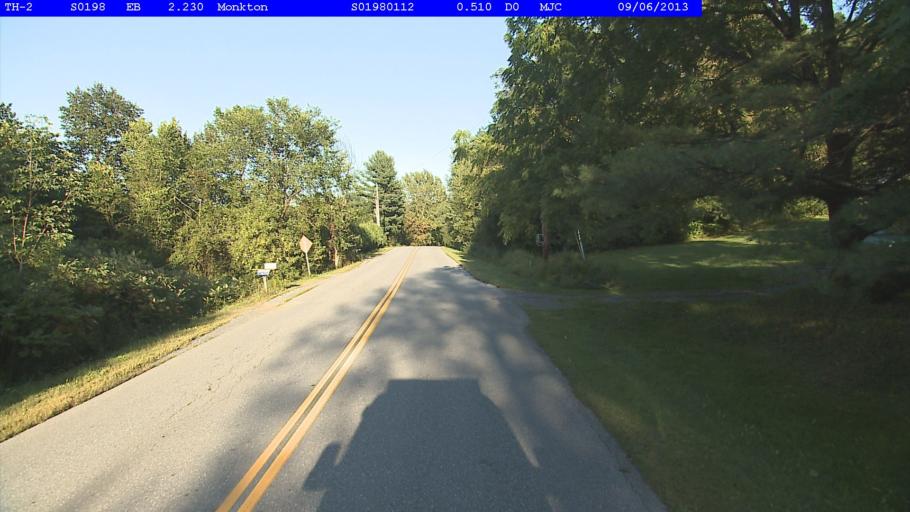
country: US
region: Vermont
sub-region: Chittenden County
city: Hinesburg
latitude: 44.2540
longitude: -73.1852
